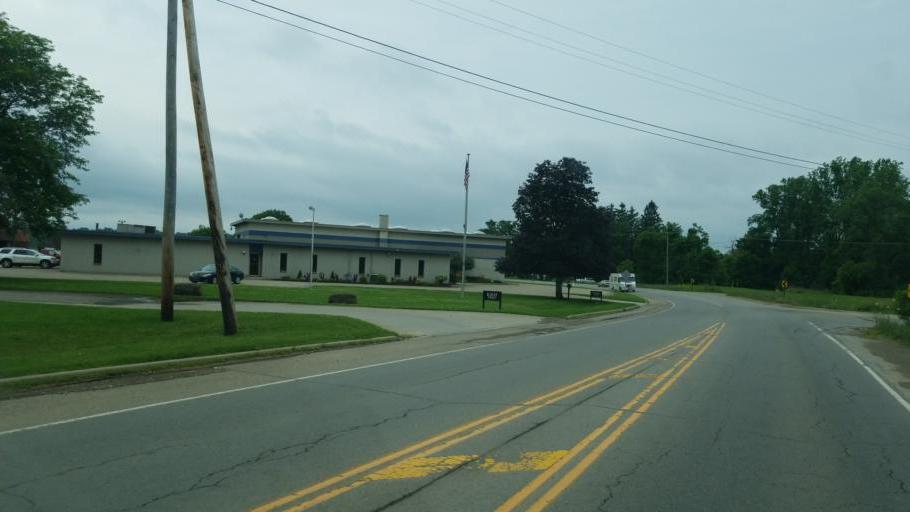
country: US
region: Ohio
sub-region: Richland County
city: Lexington
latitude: 40.6955
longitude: -82.5869
